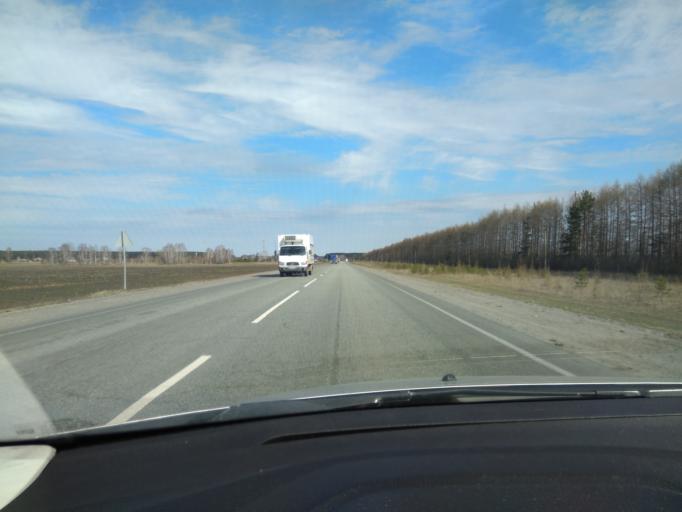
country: RU
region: Sverdlovsk
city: Troitskiy
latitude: 57.0863
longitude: 63.7159
